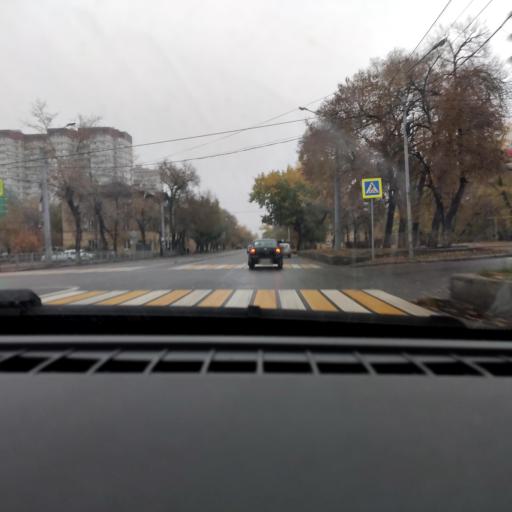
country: RU
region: Voronezj
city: Maslovka
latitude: 51.6148
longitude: 39.2473
